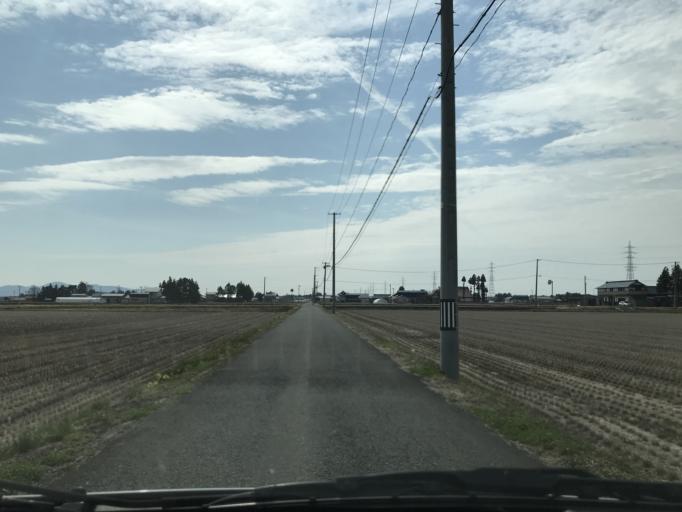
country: JP
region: Iwate
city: Mizusawa
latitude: 39.1511
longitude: 141.0854
